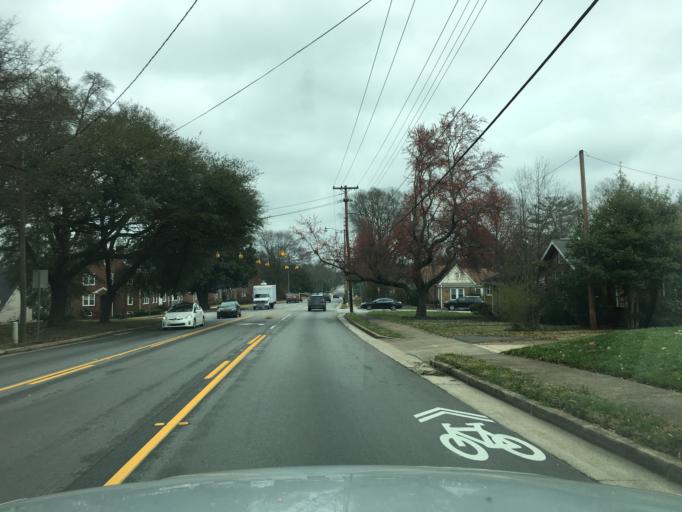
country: US
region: South Carolina
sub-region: Greenville County
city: Greenville
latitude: 34.8632
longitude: -82.3683
